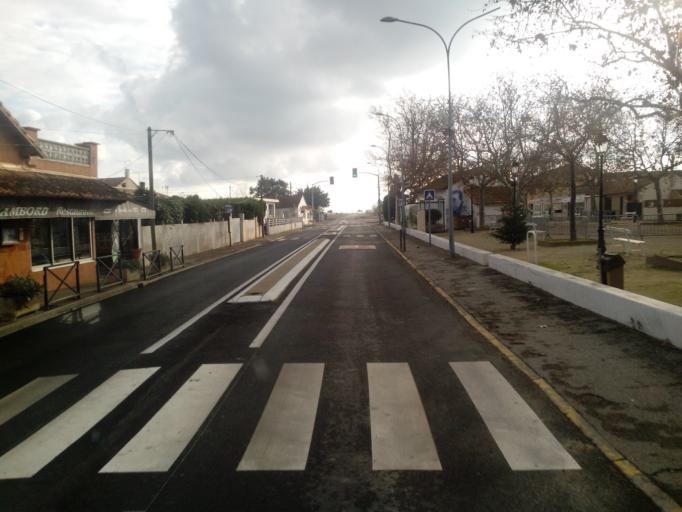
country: FR
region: Provence-Alpes-Cote d'Azur
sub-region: Departement des Bouches-du-Rhone
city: Saint-Martin-de-Crau
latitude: 43.5251
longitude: 4.7064
